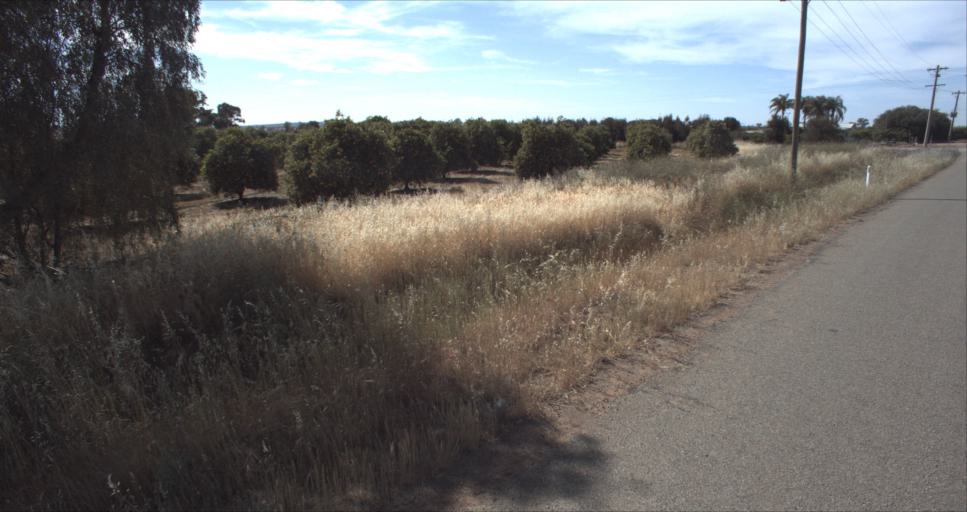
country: AU
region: New South Wales
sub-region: Leeton
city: Leeton
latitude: -34.5800
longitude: 146.4878
